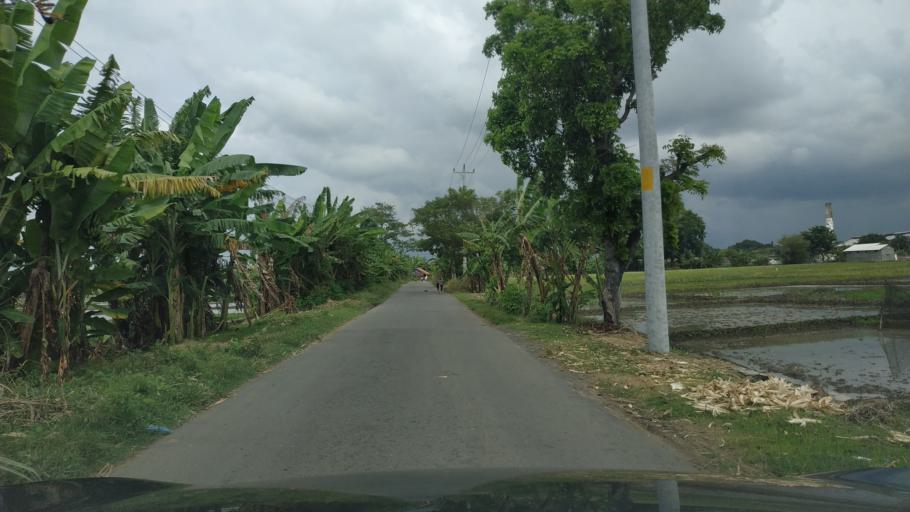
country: ID
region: Central Java
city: Pemalang
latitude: -6.9236
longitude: 109.3363
